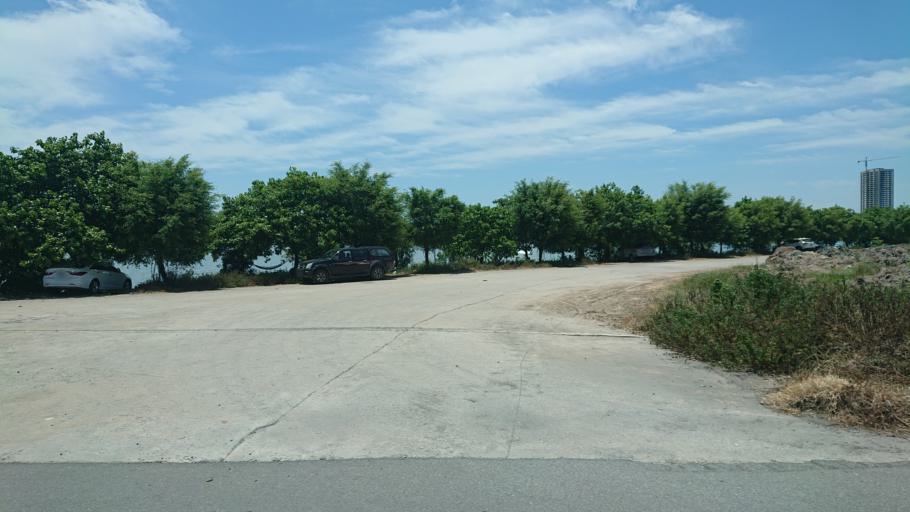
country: VN
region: Ninh Binh
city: Thanh Pho Ninh Binh
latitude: 20.2601
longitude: 105.9534
